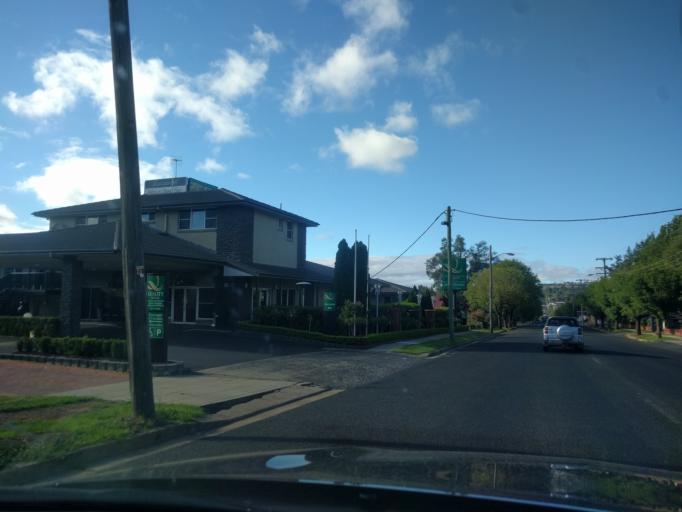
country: AU
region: New South Wales
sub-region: Armidale Dumaresq
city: Armidale
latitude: -30.5057
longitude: 151.6721
